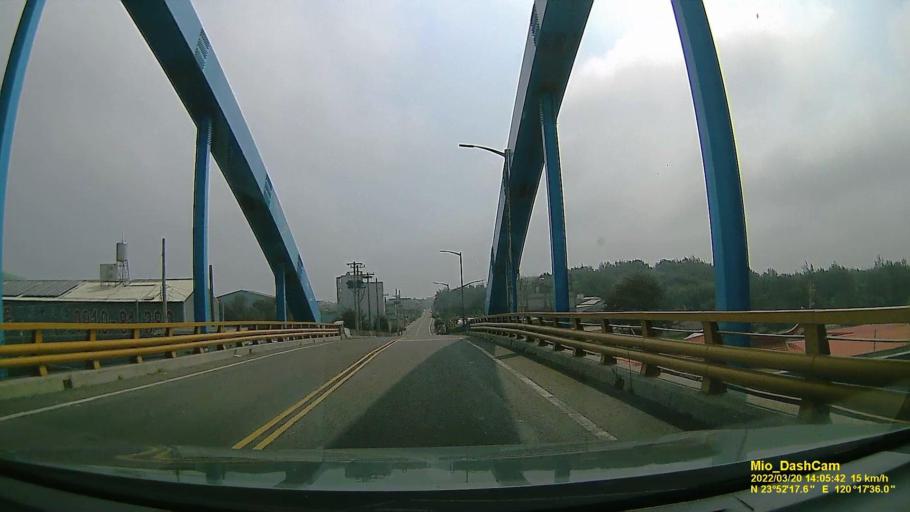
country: TW
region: Taiwan
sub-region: Yunlin
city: Douliu
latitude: 23.8715
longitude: 120.2934
